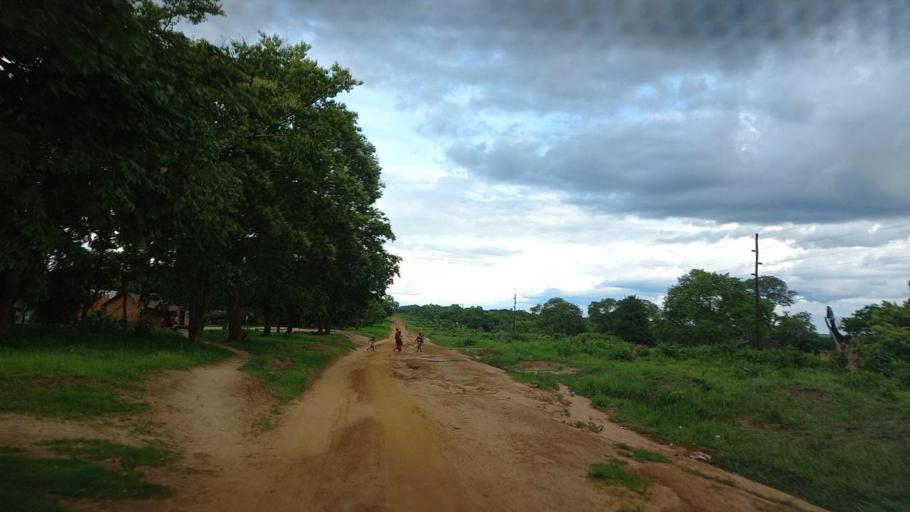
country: ZM
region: North-Western
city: Mwinilunga
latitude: -11.7733
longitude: 24.3951
